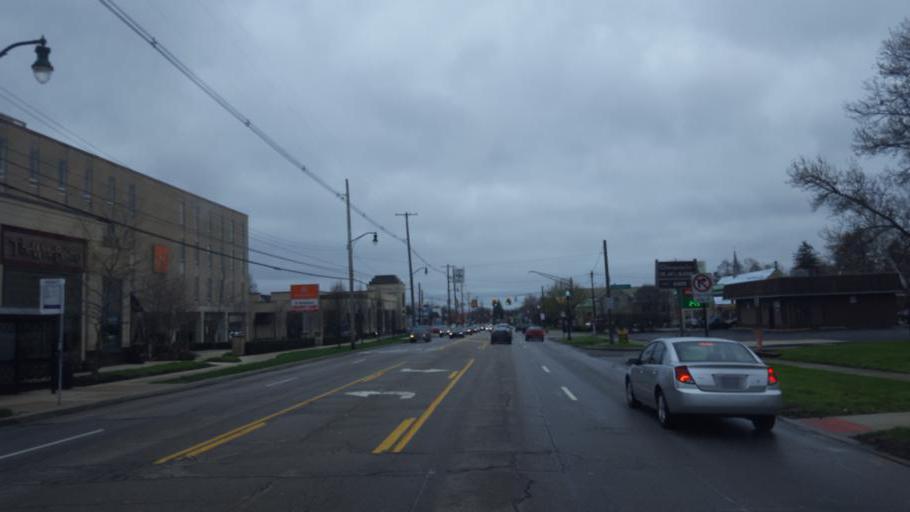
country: US
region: Ohio
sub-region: Franklin County
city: Worthington
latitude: 40.0525
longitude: -83.0201
